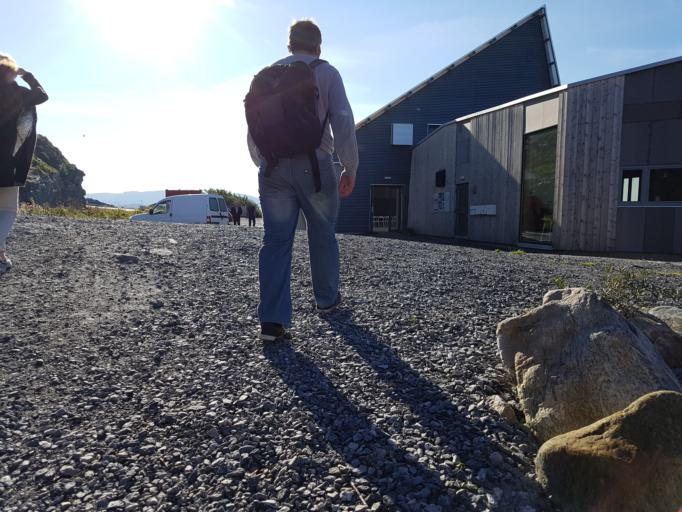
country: NO
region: Sor-Trondelag
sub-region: Afjord
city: A i Afjord
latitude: 64.0466
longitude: 9.9463
